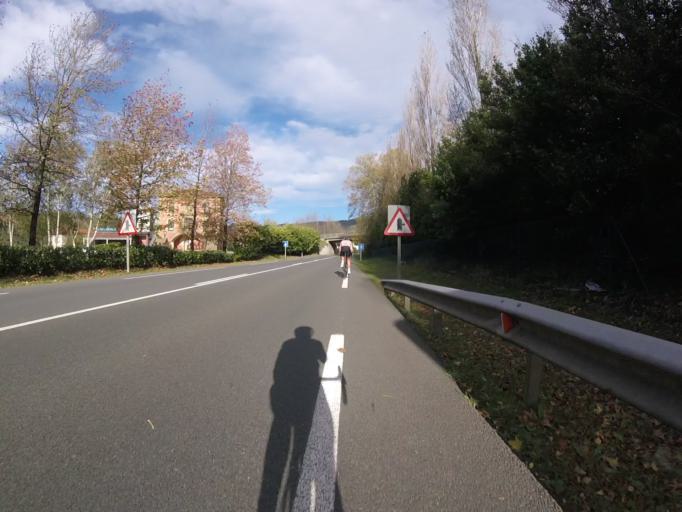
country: ES
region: Basque Country
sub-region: Provincia de Guipuzcoa
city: Usurbil
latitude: 43.2708
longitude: -2.0533
